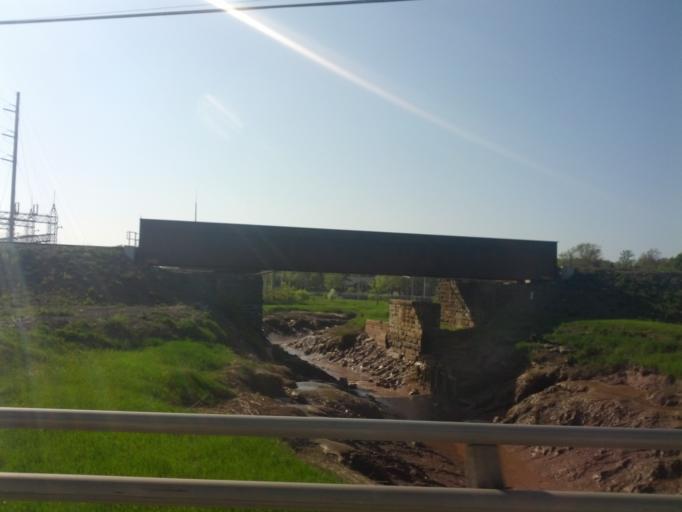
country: CA
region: New Brunswick
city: Moncton
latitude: 46.0994
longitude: -64.7763
